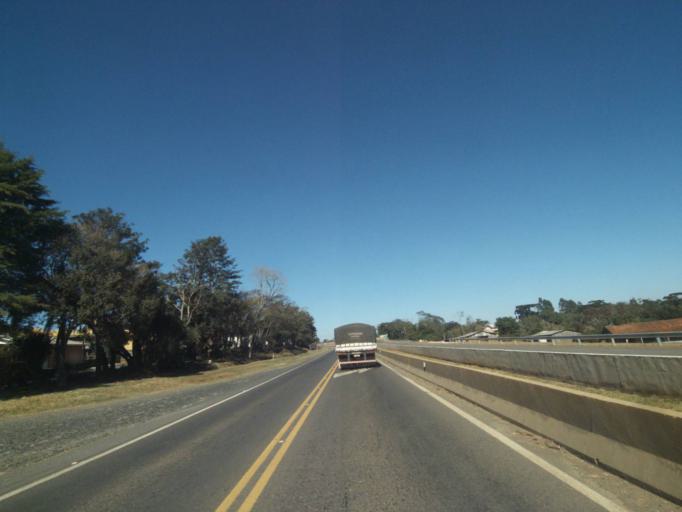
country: BR
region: Parana
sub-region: Reserva
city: Reserva
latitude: -24.6258
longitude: -50.6446
